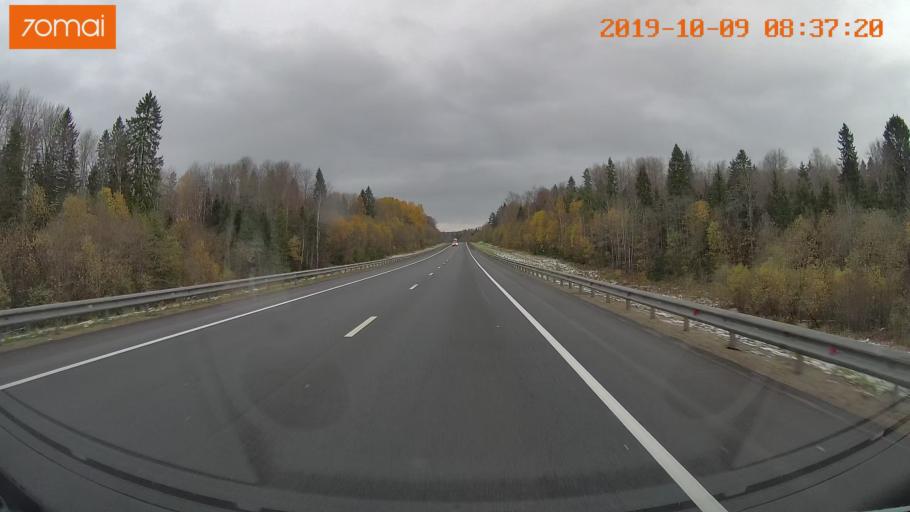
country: RU
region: Vologda
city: Gryazovets
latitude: 58.9398
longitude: 40.1748
